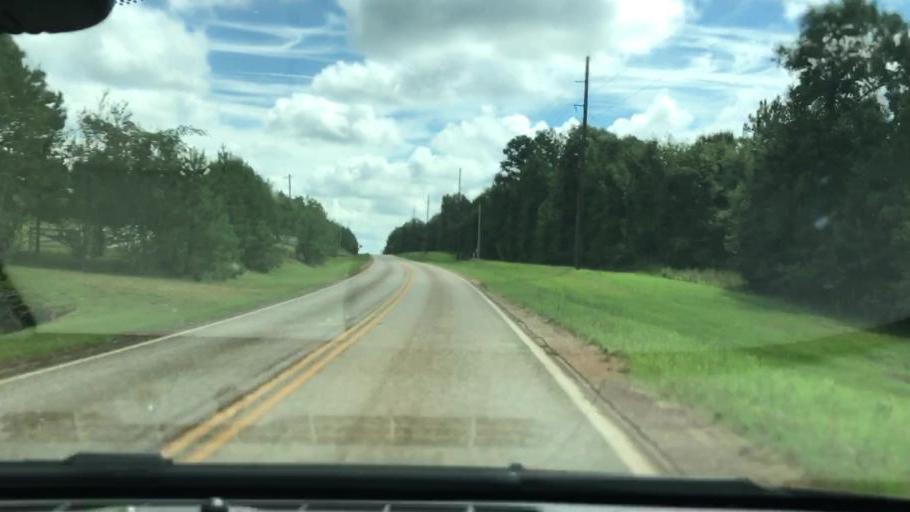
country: US
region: Georgia
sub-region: Stewart County
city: Lumpkin
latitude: 32.0630
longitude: -84.8343
